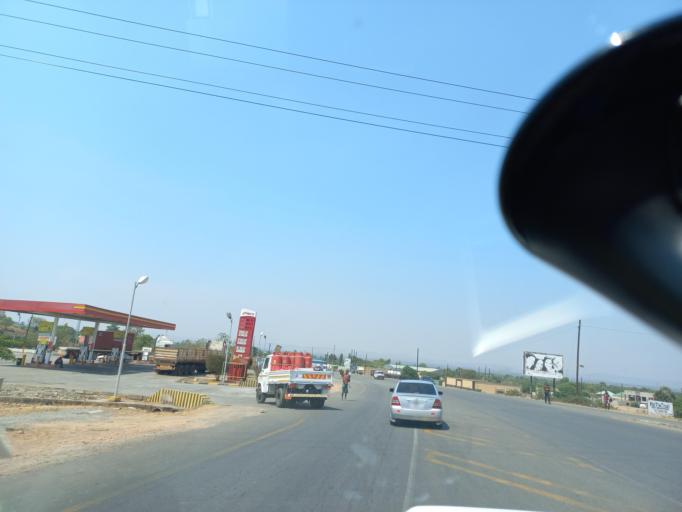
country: ZM
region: Lusaka
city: Kafue
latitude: -15.7595
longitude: 28.1790
